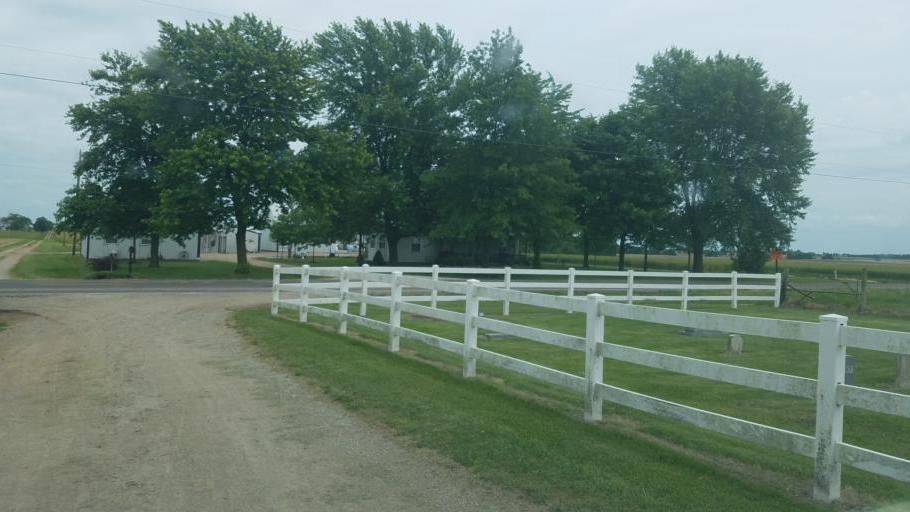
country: US
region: Missouri
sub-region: Morgan County
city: Versailles
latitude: 38.5144
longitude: -92.7435
